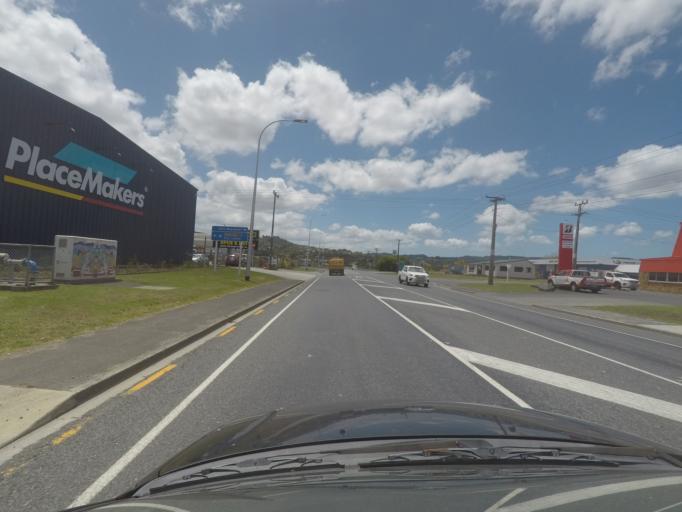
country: NZ
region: Northland
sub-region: Whangarei
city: Whangarei
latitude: -35.7404
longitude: 174.3332
